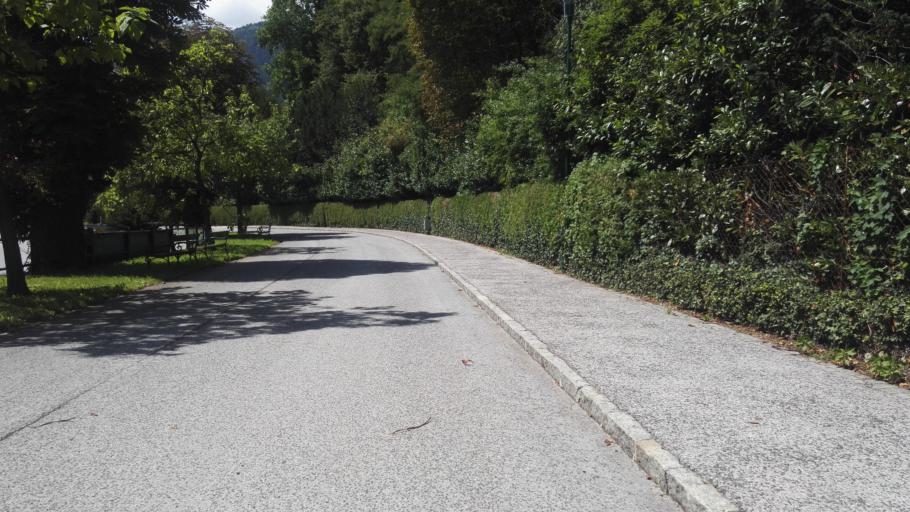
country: AT
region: Styria
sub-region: Politischer Bezirk Graz-Umgebung
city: Frohnleiten
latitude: 47.2702
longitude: 15.3228
